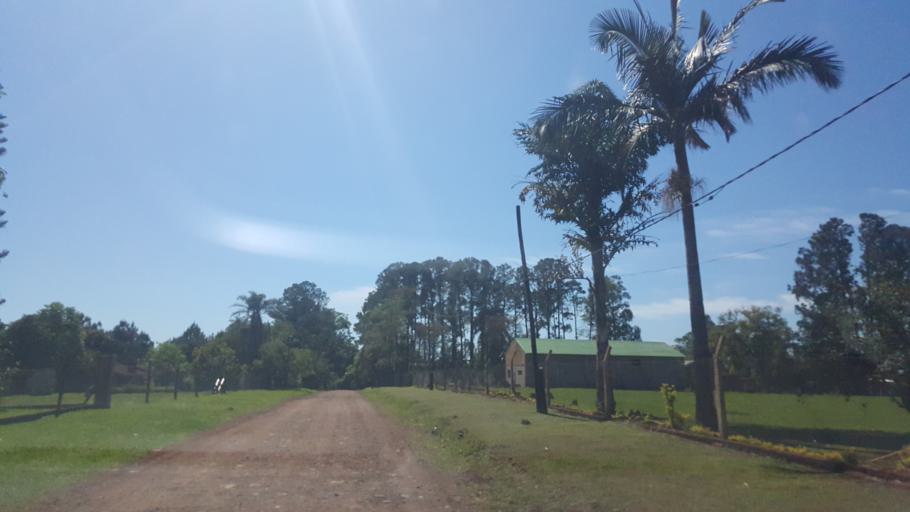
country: AR
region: Misiones
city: Garupa
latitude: -27.4870
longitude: -55.8618
